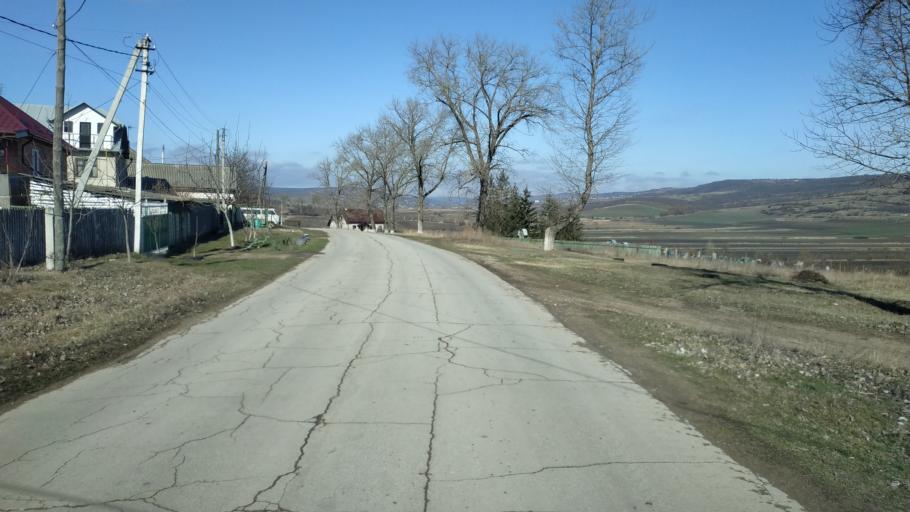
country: MD
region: Hincesti
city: Hincesti
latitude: 46.9751
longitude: 28.5757
